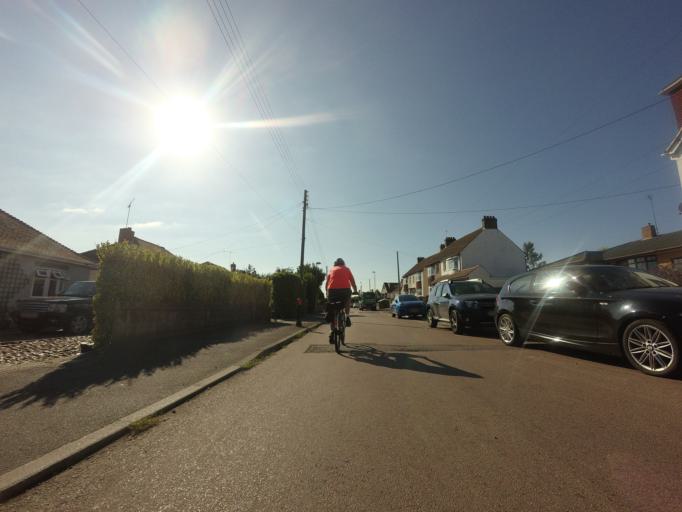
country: GB
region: England
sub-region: Kent
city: Strood
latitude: 51.4138
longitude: 0.5101
